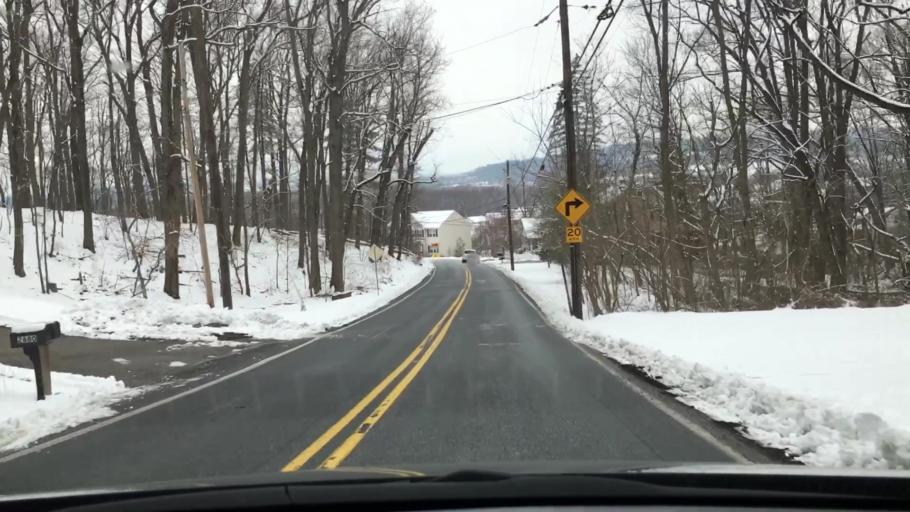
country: US
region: Pennsylvania
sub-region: York County
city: Emigsville
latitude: 40.0070
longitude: -76.7045
